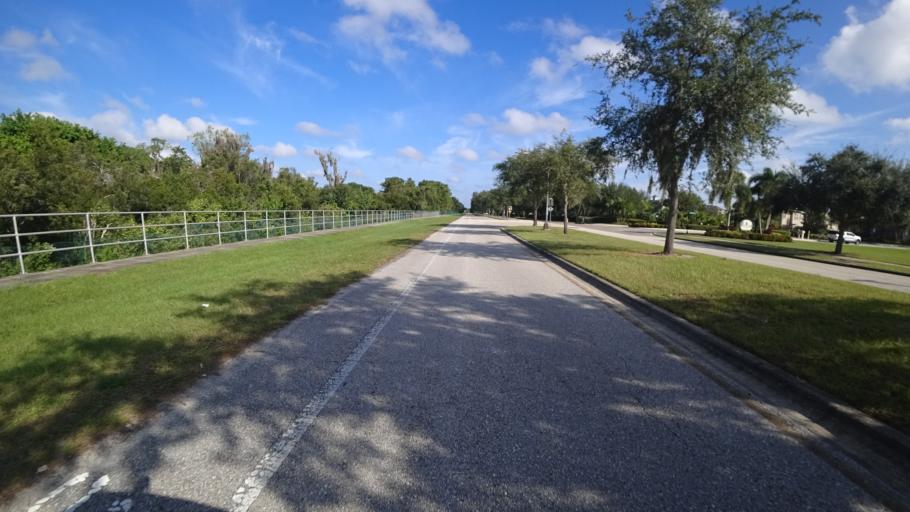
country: US
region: Florida
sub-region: Sarasota County
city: The Meadows
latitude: 27.3959
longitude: -82.4631
